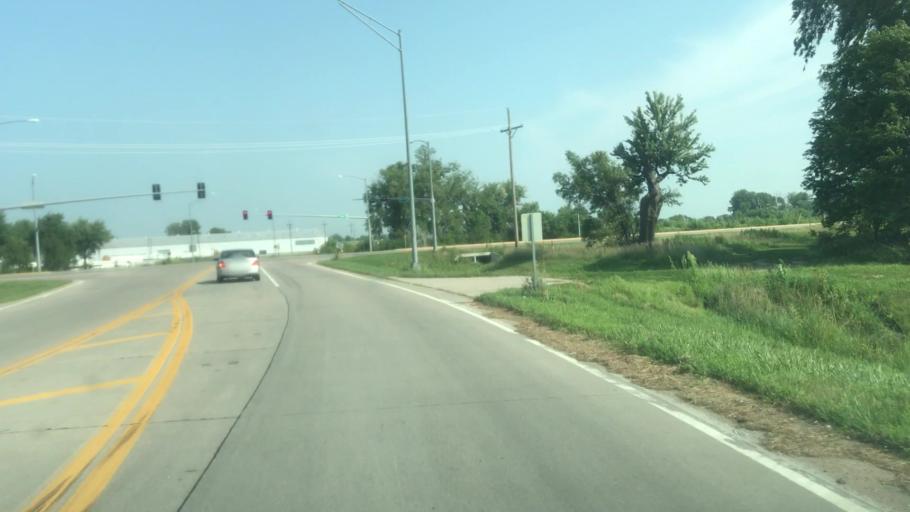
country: US
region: Nebraska
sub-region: Hall County
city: Grand Island
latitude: 40.9377
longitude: -98.3004
